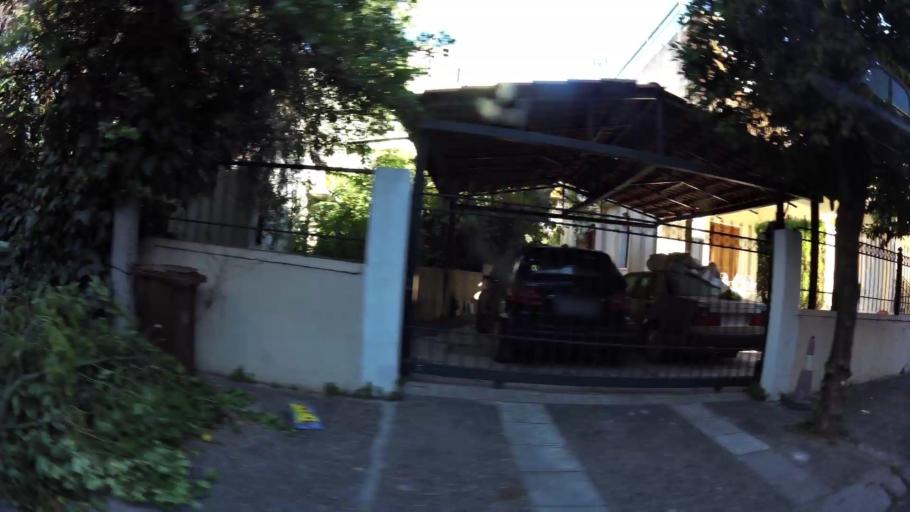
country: GR
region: Attica
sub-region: Nomarchia Athinas
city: Khalandrion
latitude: 38.0167
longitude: 23.7996
